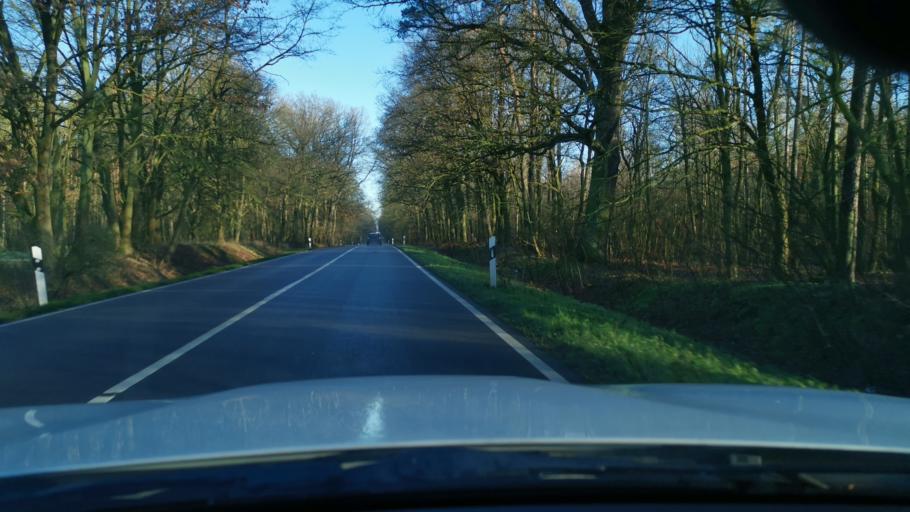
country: DE
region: Saxony-Anhalt
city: Kropstadt
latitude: 51.9445
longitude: 12.7244
